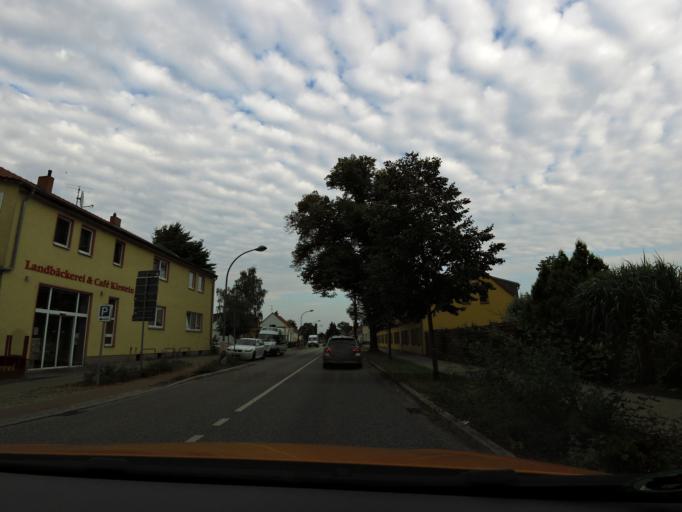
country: DE
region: Brandenburg
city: Gross Kreutz
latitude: 52.4035
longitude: 12.7770
